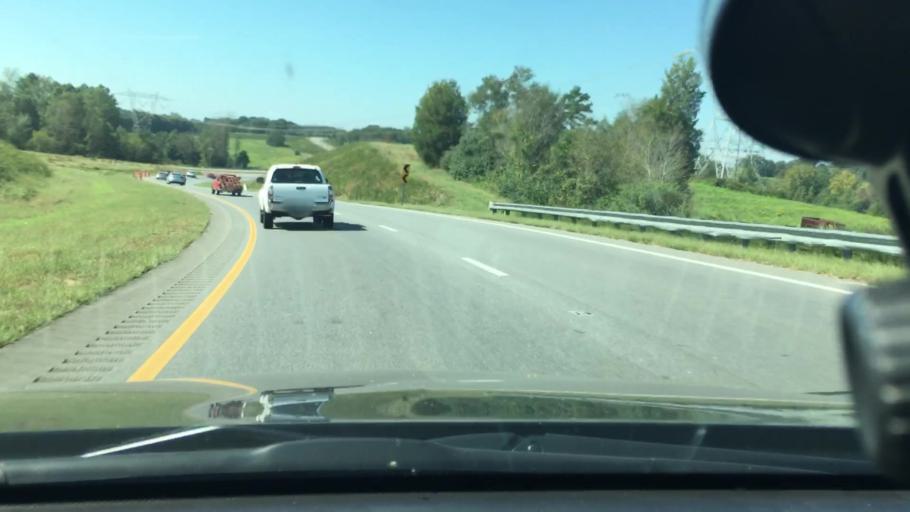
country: US
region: North Carolina
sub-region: Cleveland County
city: Boiling Springs
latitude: 35.2979
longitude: -81.6594
